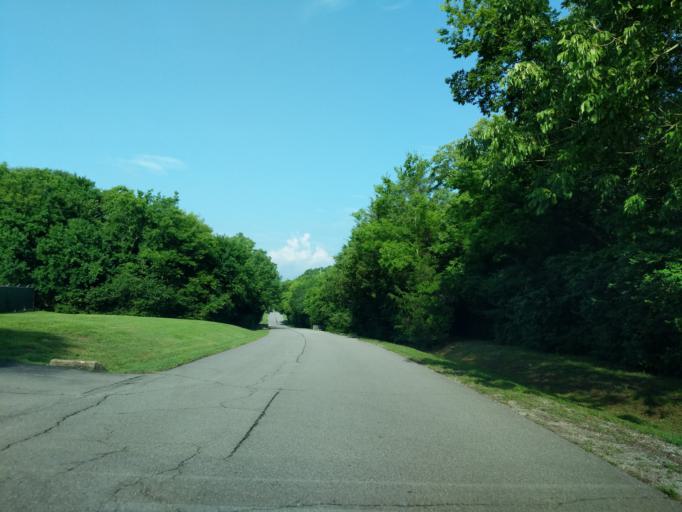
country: US
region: Tennessee
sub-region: Sumner County
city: Hendersonville
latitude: 36.3003
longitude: -86.6517
